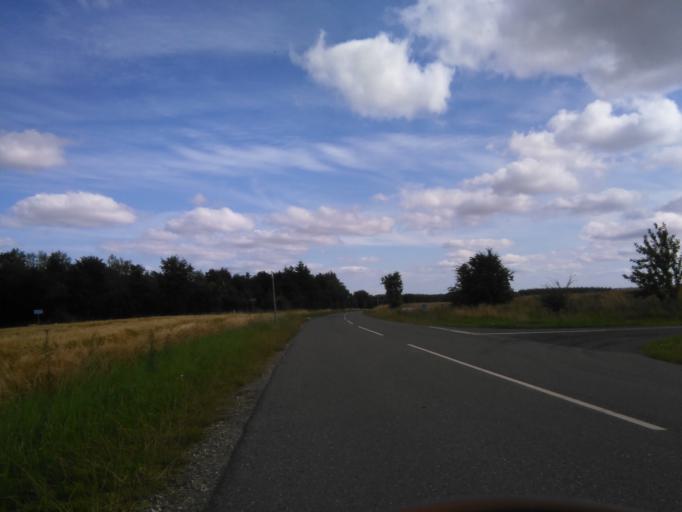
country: DK
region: Central Jutland
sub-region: Skanderborg Kommune
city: Horning
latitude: 56.0977
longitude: 10.0188
